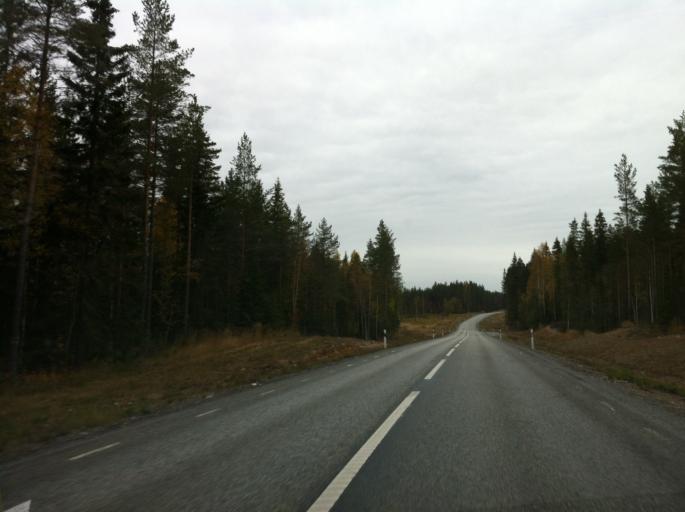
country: SE
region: OErebro
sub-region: Ljusnarsbergs Kommun
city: Kopparberg
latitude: 59.9670
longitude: 15.0201
